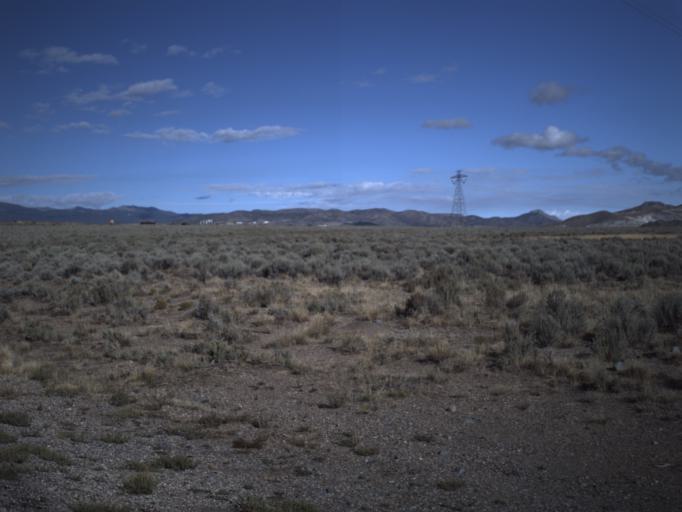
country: US
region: Utah
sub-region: Beaver County
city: Milford
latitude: 38.4092
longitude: -113.0596
